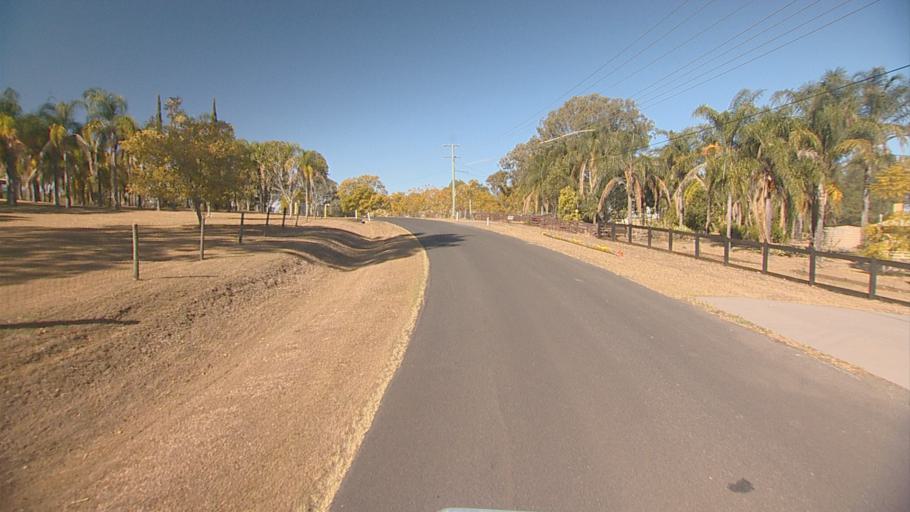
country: AU
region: Queensland
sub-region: Logan
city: Cedar Vale
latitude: -27.8918
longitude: 152.9774
